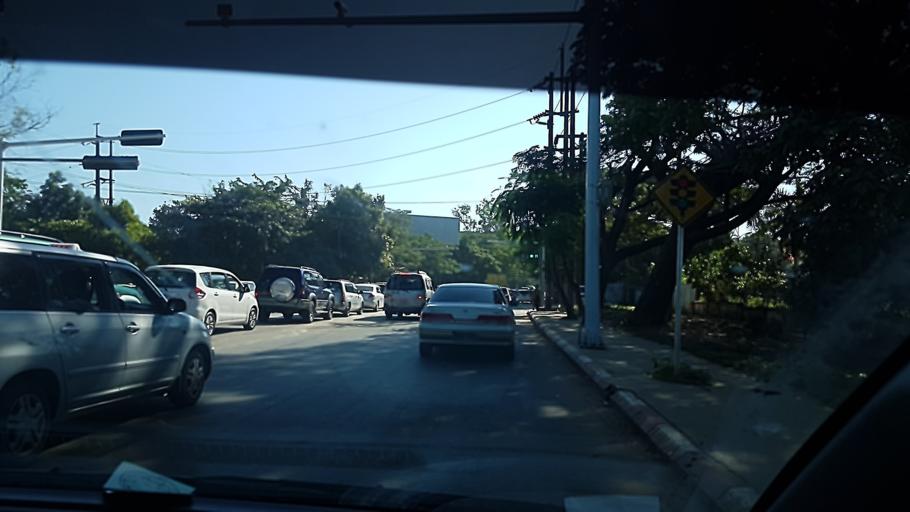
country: MM
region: Yangon
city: Yangon
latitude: 16.8575
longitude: 96.1292
